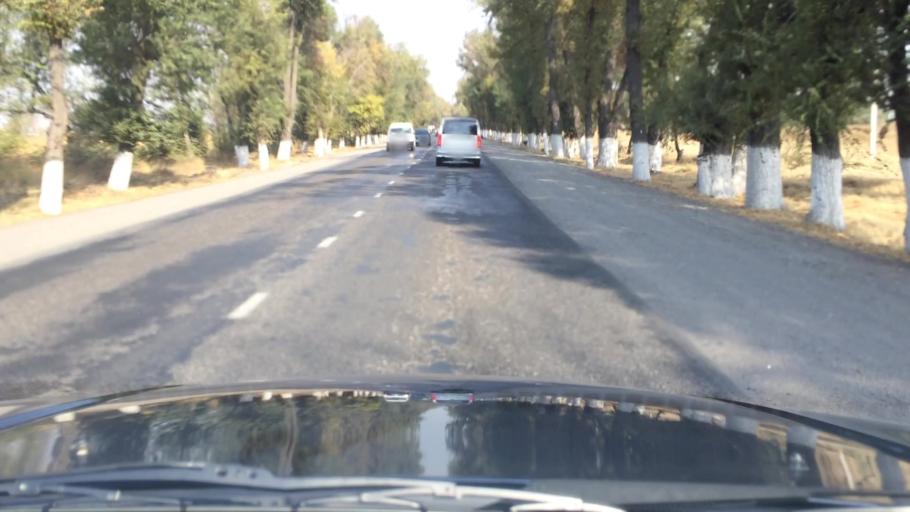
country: KG
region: Chuy
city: Lebedinovka
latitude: 42.9271
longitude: 74.6908
